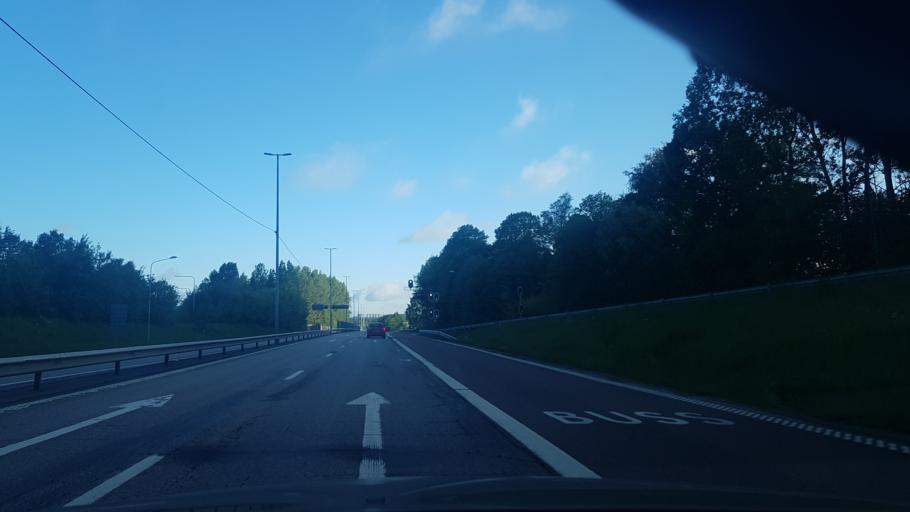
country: SE
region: Vaestra Goetaland
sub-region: Goteborg
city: Billdal
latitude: 57.6144
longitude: 11.9410
